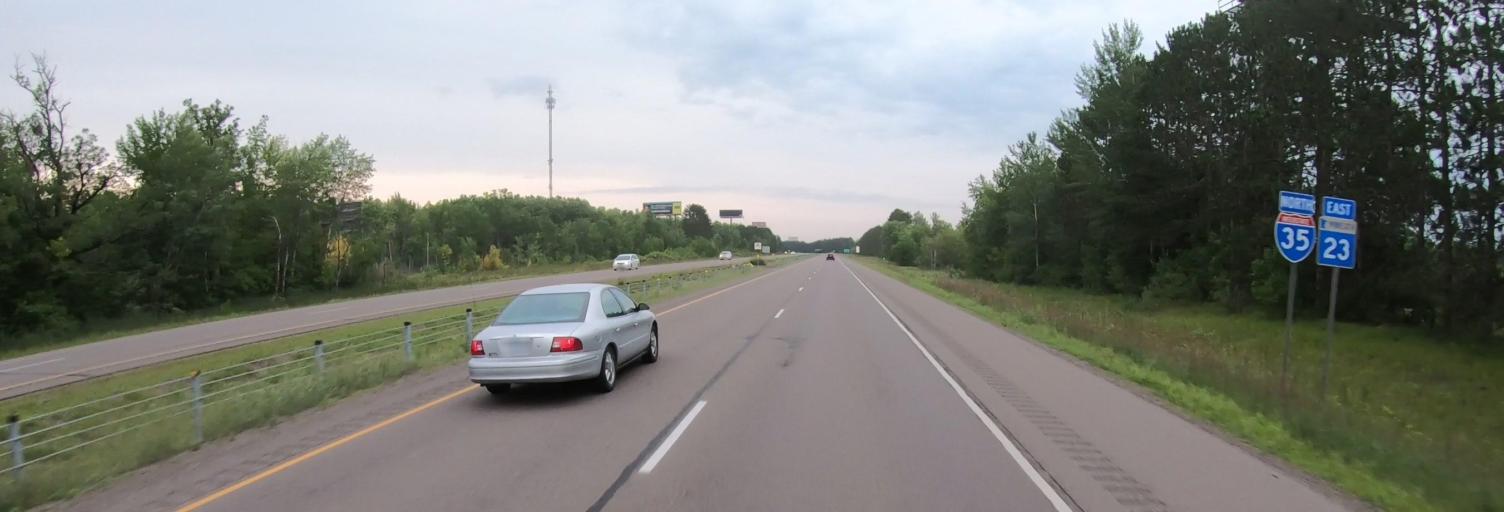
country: US
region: Minnesota
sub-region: Pine County
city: Hinckley
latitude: 46.0177
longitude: -92.9285
